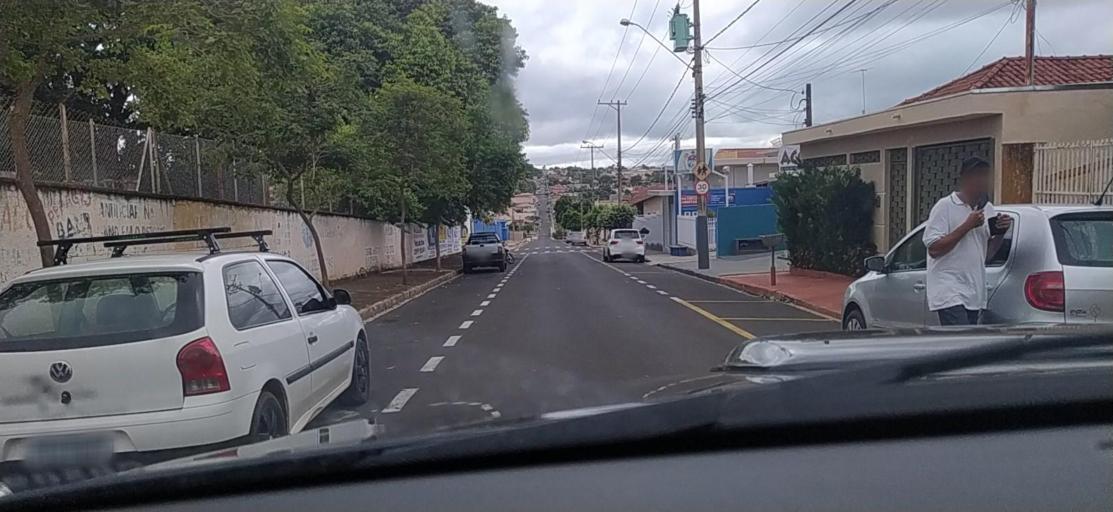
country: BR
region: Sao Paulo
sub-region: Olimpia
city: Olimpia
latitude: -20.7352
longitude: -48.9160
